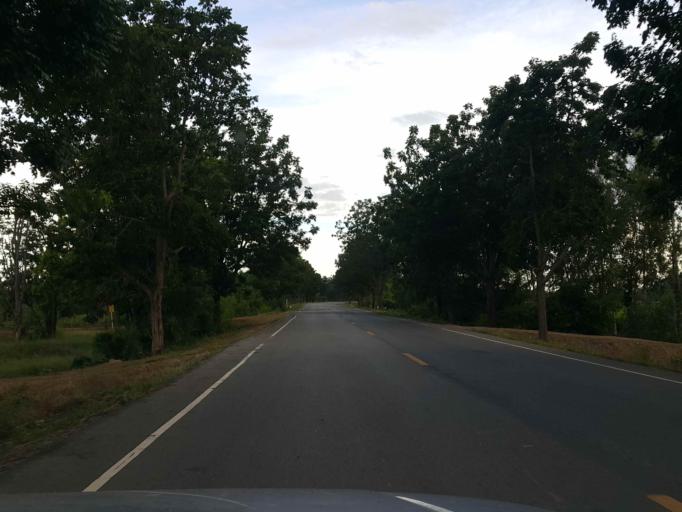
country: TH
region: Sukhothai
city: Sawankhalok
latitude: 17.3438
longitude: 99.7428
